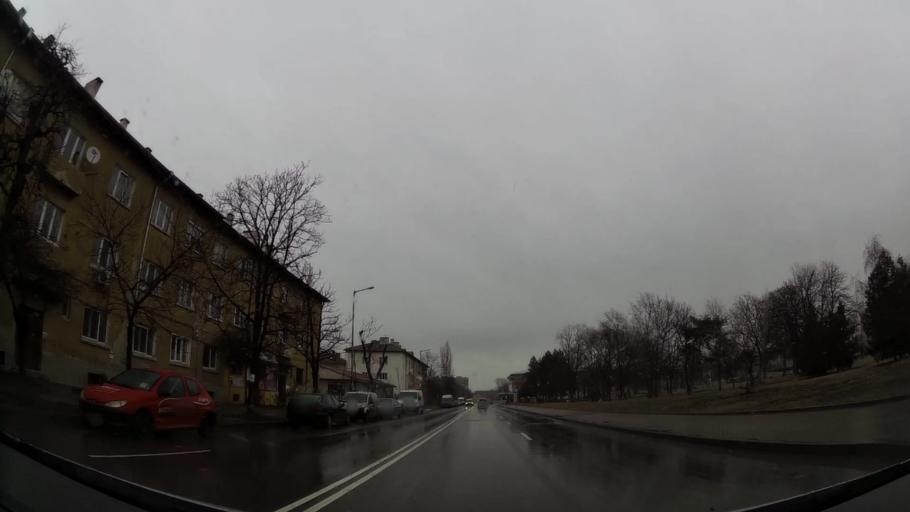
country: BG
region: Sofia-Capital
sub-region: Stolichna Obshtina
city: Sofia
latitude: 42.6643
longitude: 23.3987
